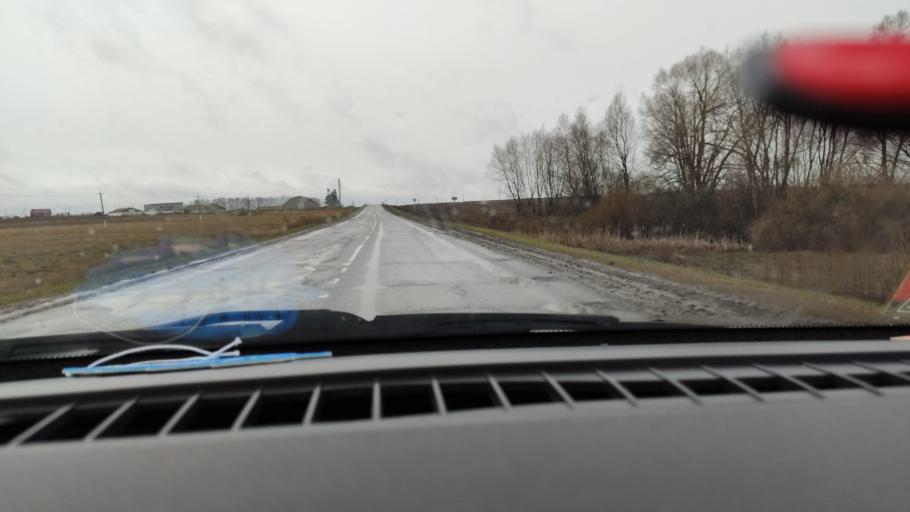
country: RU
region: Tatarstan
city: Nurlat
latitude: 54.6034
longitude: 50.8884
